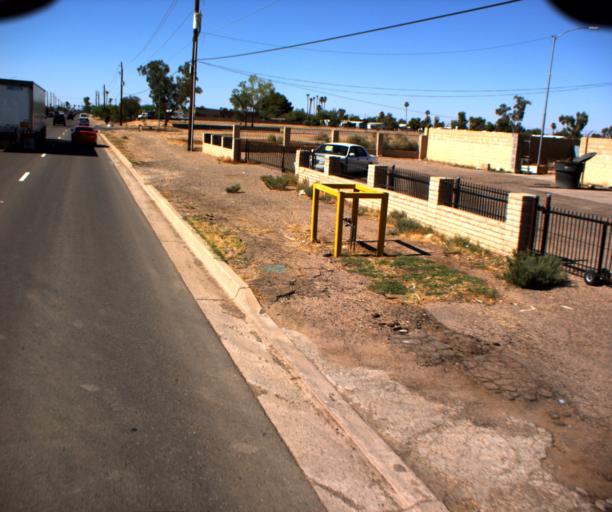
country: US
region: Arizona
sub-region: Pinal County
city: Casa Grande
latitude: 32.8988
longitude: -111.7574
